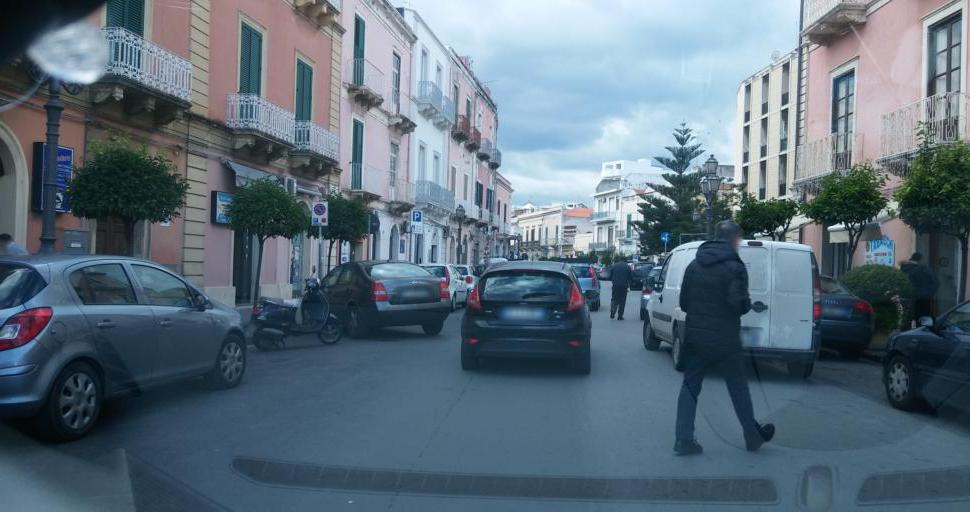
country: IT
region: Sicily
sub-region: Messina
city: Milazzo
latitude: 38.2199
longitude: 15.2409
